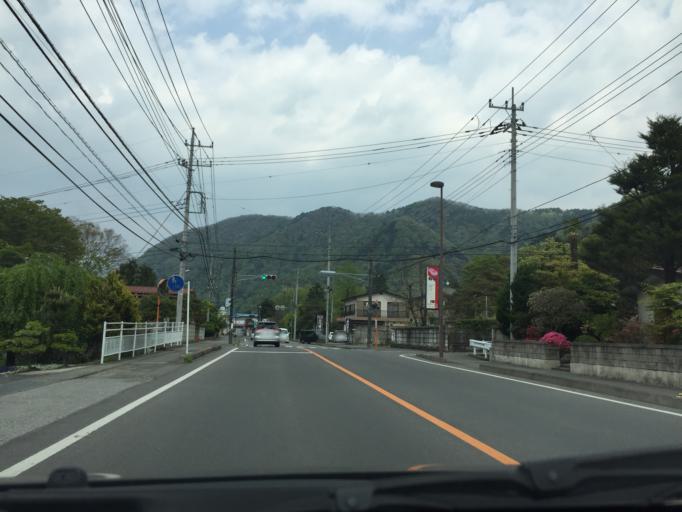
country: JP
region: Tochigi
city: Imaichi
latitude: 36.8163
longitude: 139.7150
